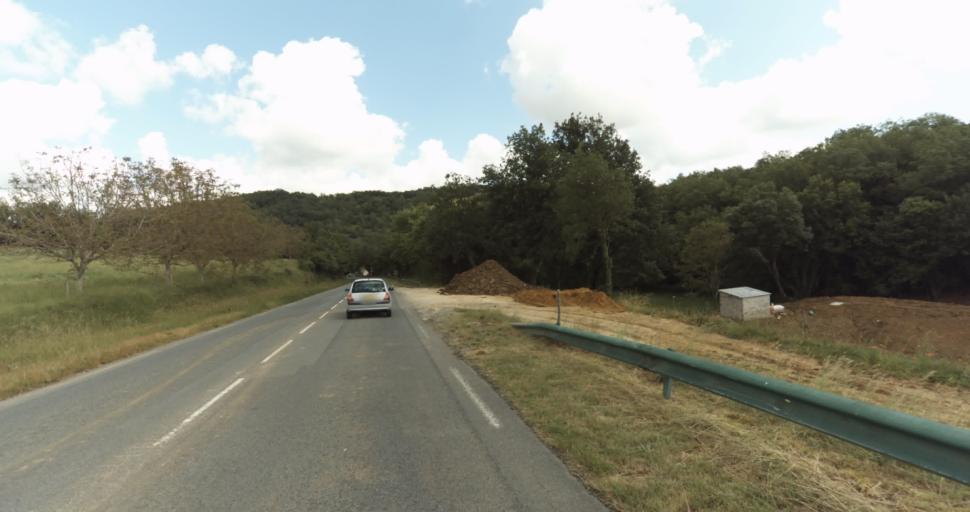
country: FR
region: Aquitaine
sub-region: Departement de la Dordogne
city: Beaumont-du-Perigord
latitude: 44.7832
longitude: 0.7661
